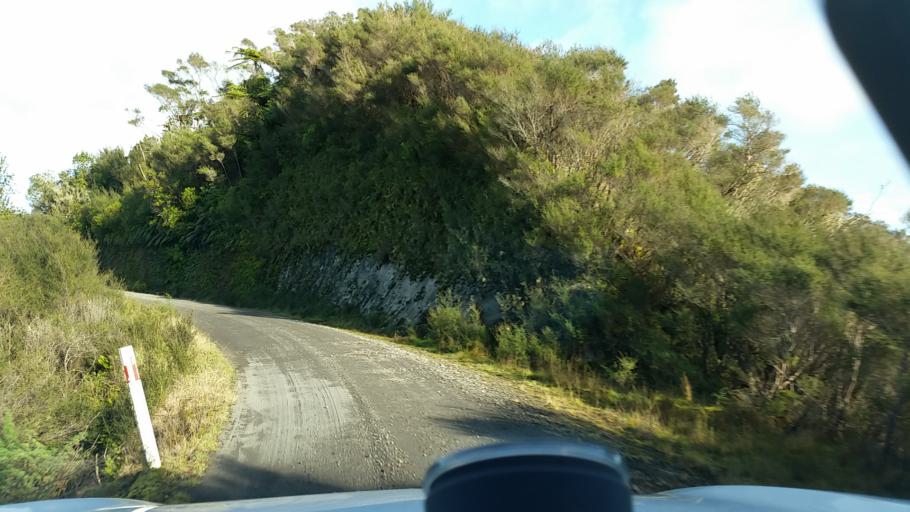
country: NZ
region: Taranaki
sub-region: South Taranaki District
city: Eltham
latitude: -39.4067
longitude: 174.5562
